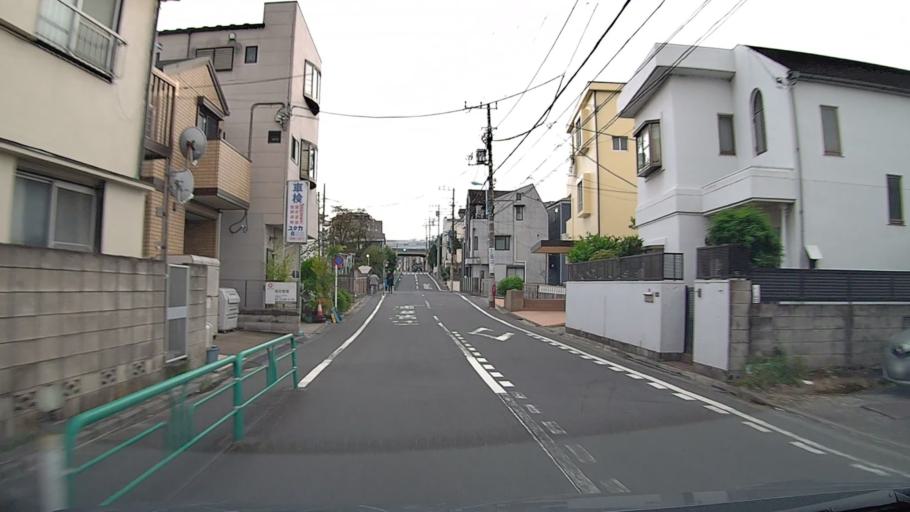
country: JP
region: Tokyo
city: Musashino
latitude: 35.7055
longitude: 139.6100
